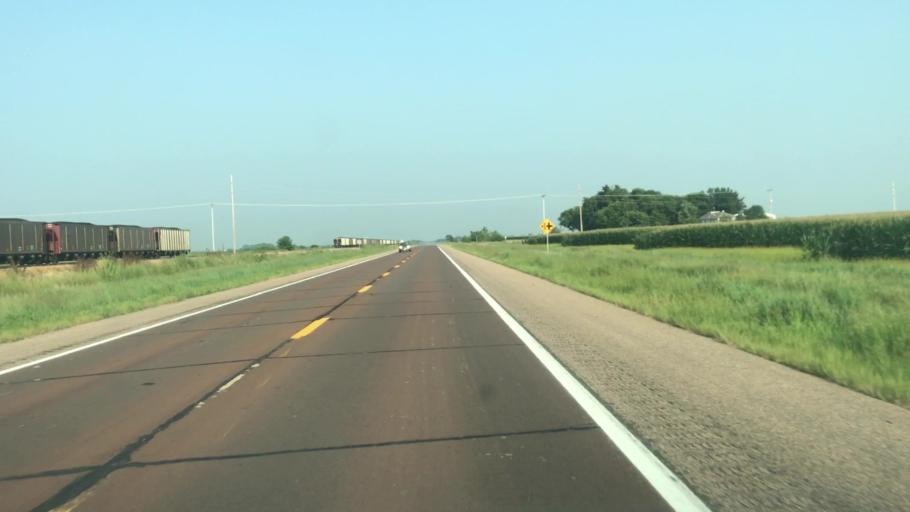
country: US
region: Nebraska
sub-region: Hall County
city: Wood River
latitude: 40.9986
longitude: -98.5915
